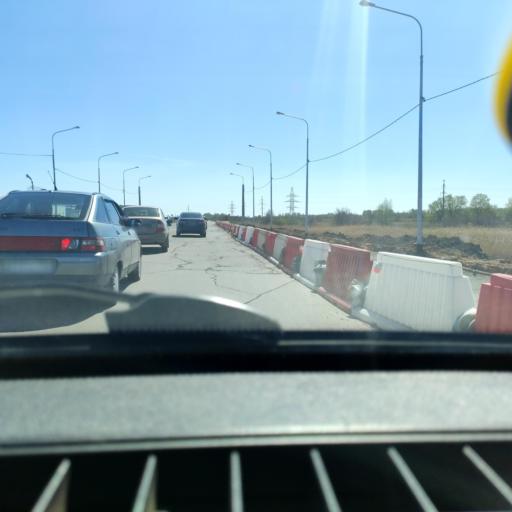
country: RU
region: Samara
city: Tol'yatti
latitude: 53.6770
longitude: 49.4150
